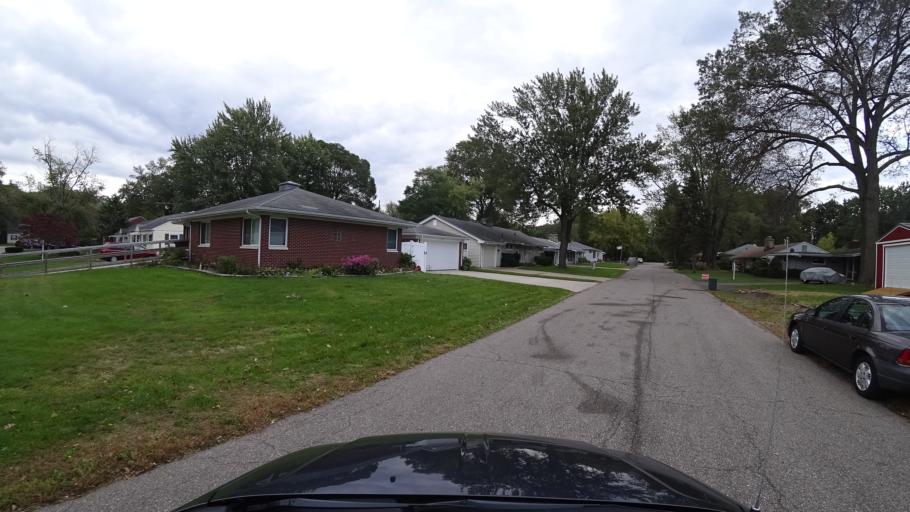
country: US
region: Indiana
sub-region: LaPorte County
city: Michigan City
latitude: 41.6976
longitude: -86.8883
